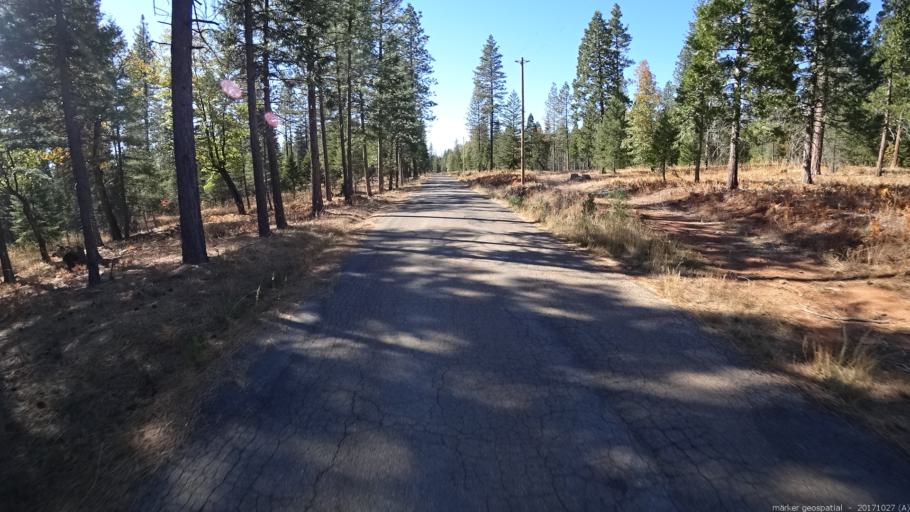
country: US
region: California
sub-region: Shasta County
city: Shingletown
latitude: 40.6143
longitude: -121.8264
